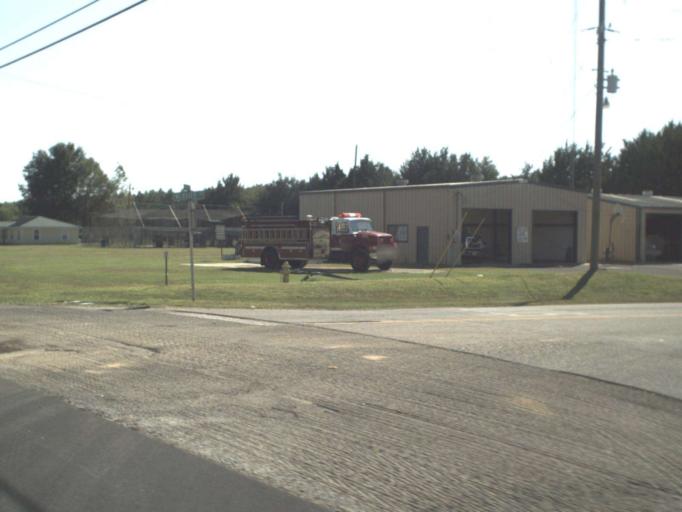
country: US
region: Alabama
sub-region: Covington County
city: Florala
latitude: 30.9699
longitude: -86.3020
